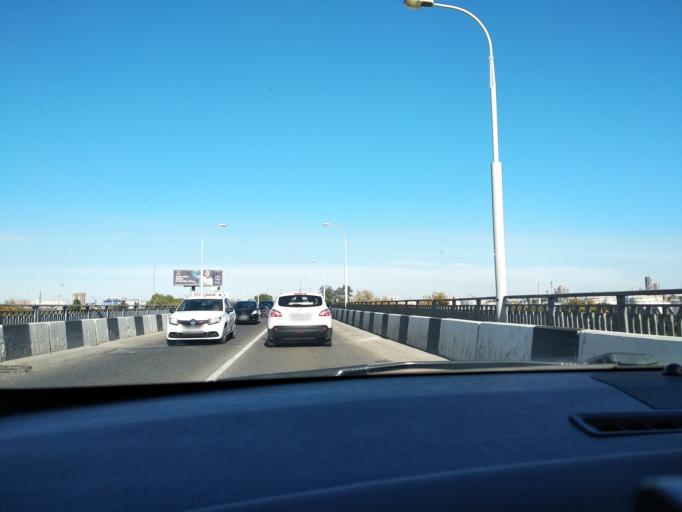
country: RU
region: Adygeya
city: Yablonovskiy
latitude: 44.9955
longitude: 38.9572
